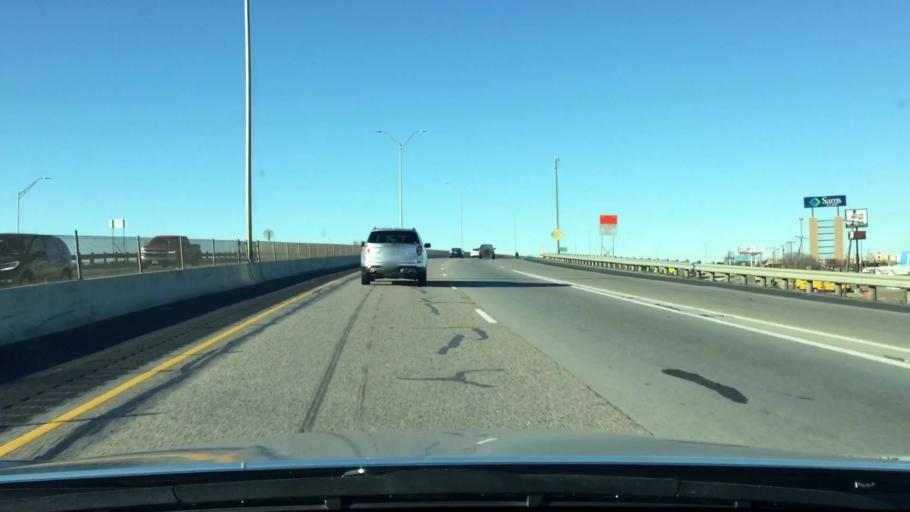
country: US
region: Texas
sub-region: Johnson County
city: Burleson
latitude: 32.5511
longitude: -97.3185
